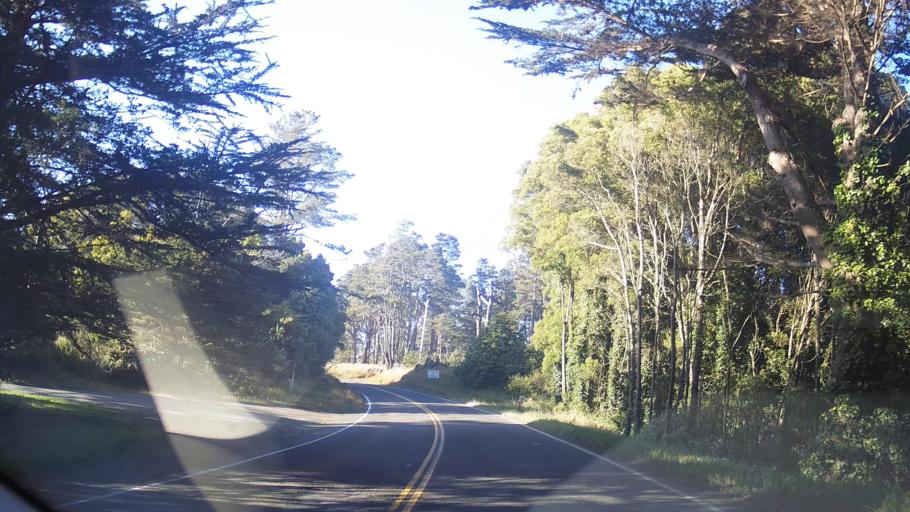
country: US
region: California
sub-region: Mendocino County
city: Fort Bragg
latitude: 39.4713
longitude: -123.7982
